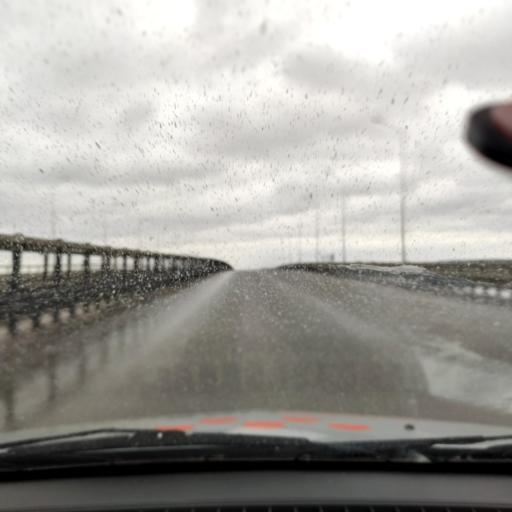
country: RU
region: Bashkortostan
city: Ufa
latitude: 54.6839
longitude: 55.9977
